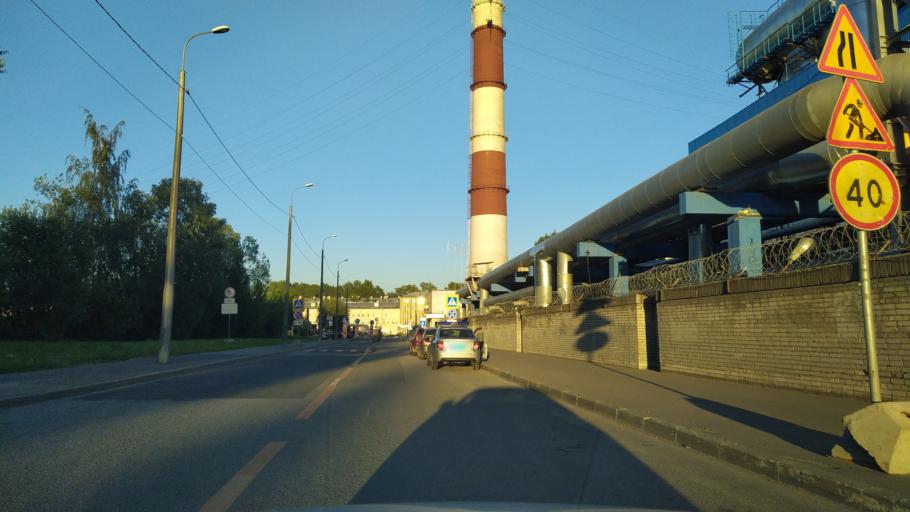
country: RU
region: Leningrad
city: Finlyandskiy
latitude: 59.9709
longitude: 30.3765
